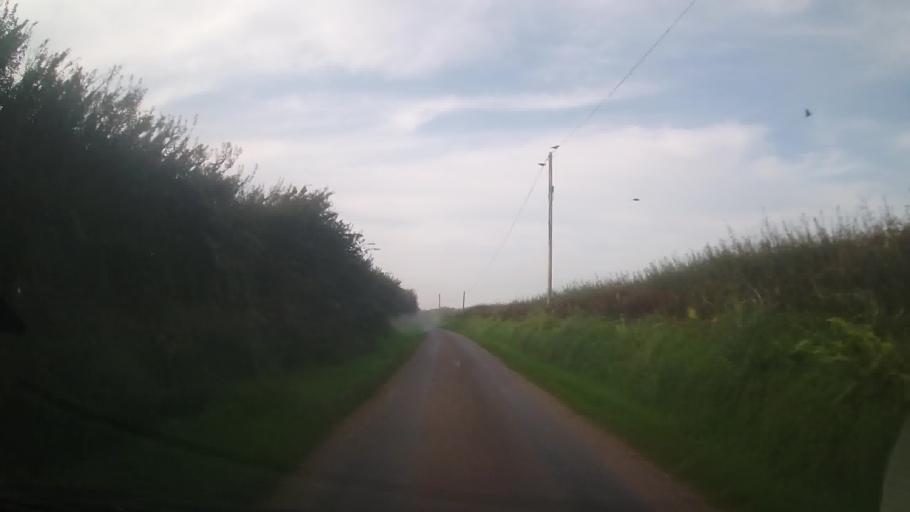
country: GB
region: Wales
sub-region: Pembrokeshire
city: Camrose
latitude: 51.8847
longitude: -5.0529
